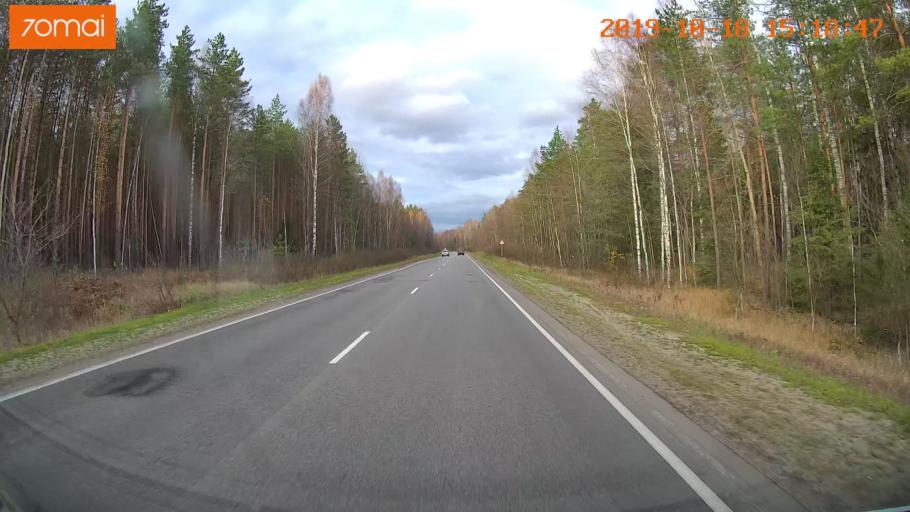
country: RU
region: Vladimir
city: Anopino
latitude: 55.6638
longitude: 40.7322
